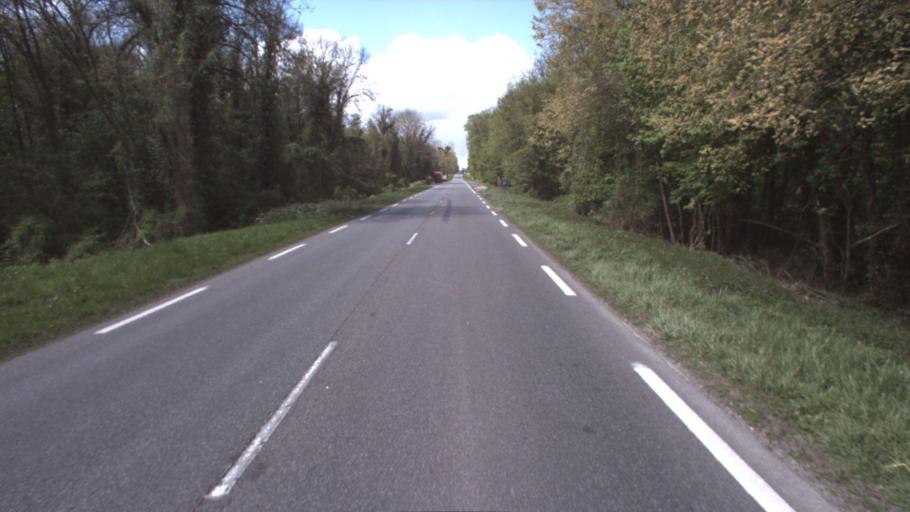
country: FR
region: Ile-de-France
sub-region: Departement de Seine-et-Marne
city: La Ferte-Gaucher
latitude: 48.6927
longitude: 3.3240
